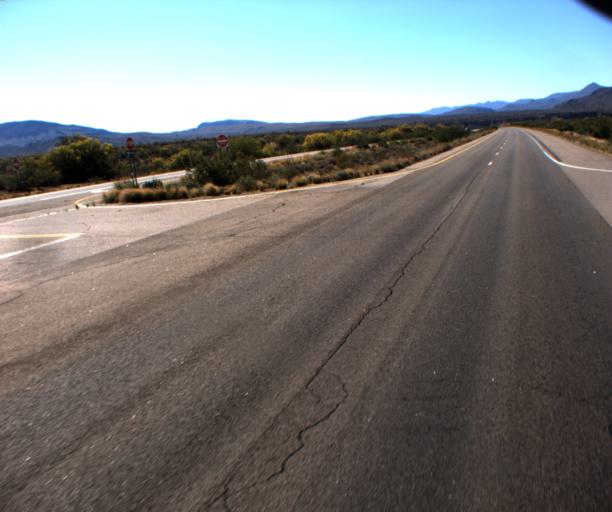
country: US
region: Arizona
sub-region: Yavapai County
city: Bagdad
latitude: 34.6533
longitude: -113.5740
